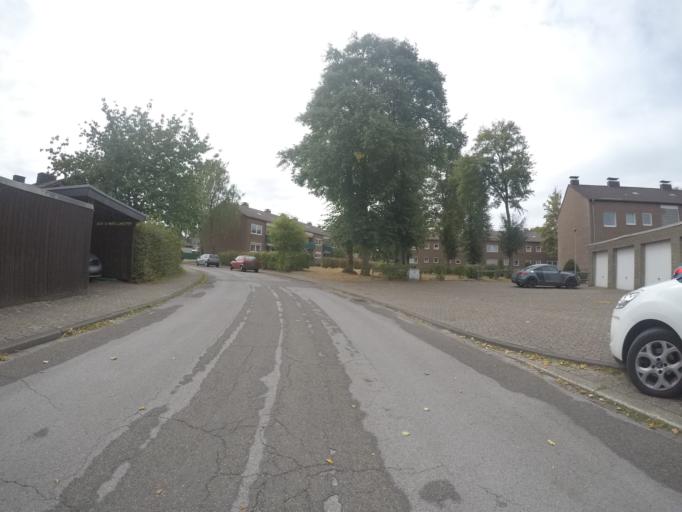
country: DE
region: North Rhine-Westphalia
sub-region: Regierungsbezirk Dusseldorf
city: Bocholt
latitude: 51.8410
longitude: 6.5931
